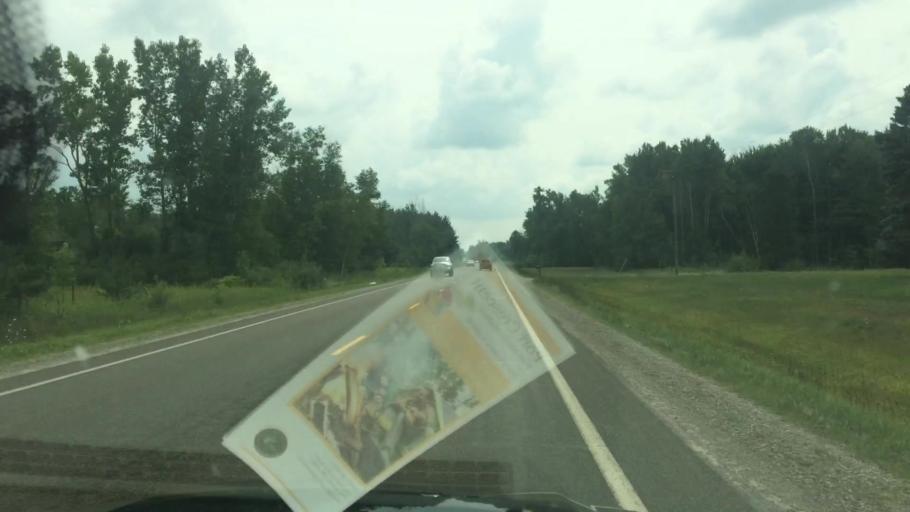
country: US
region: Michigan
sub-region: Tuscola County
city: Cass City
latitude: 43.6526
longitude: -83.0983
